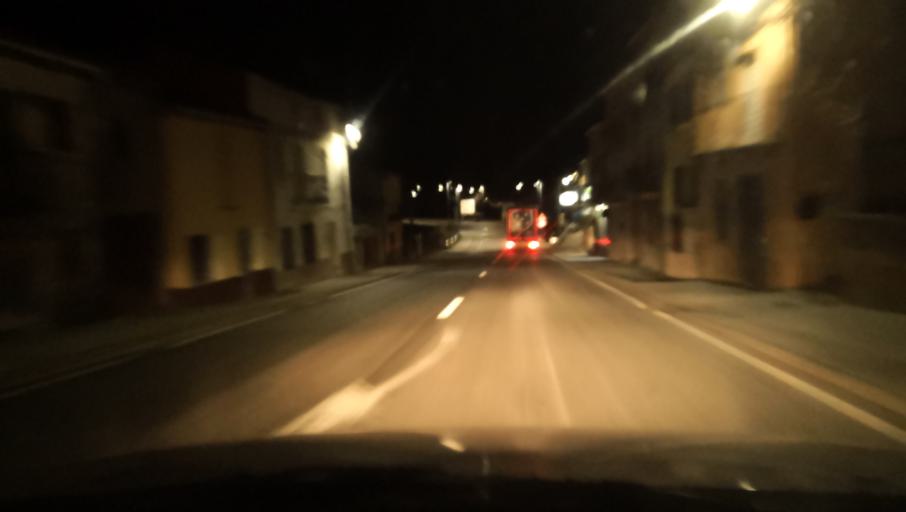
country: ES
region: Castille and Leon
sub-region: Provincia de Zamora
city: Alcanices
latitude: 41.6994
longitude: -6.3485
